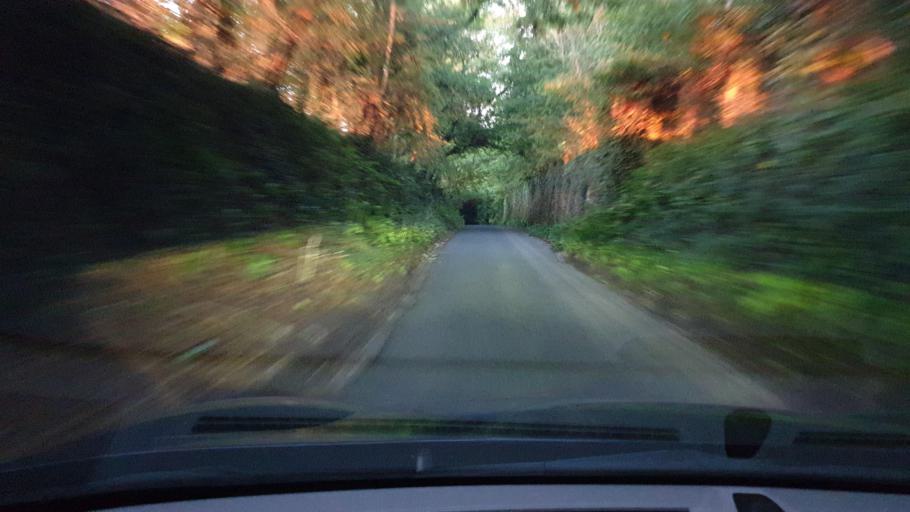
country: IE
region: Leinster
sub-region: Kildare
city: Prosperous
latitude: 53.3463
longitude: -6.7547
